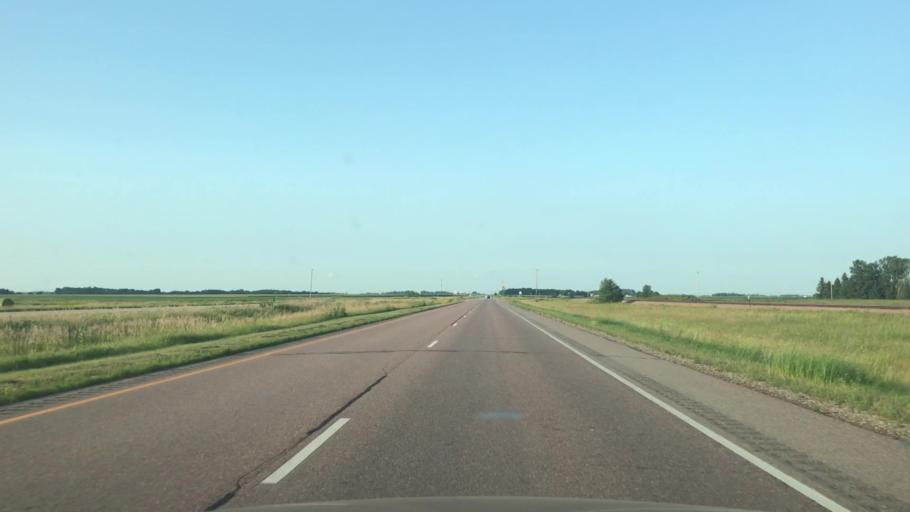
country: US
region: Minnesota
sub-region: Nobles County
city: Worthington
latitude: 43.7449
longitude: -95.4002
